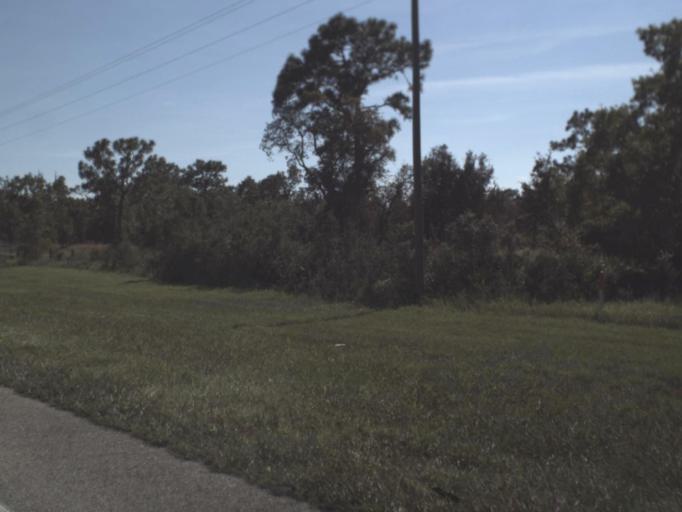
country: US
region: Florida
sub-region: Highlands County
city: Lake Placid
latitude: 27.3826
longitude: -81.4082
